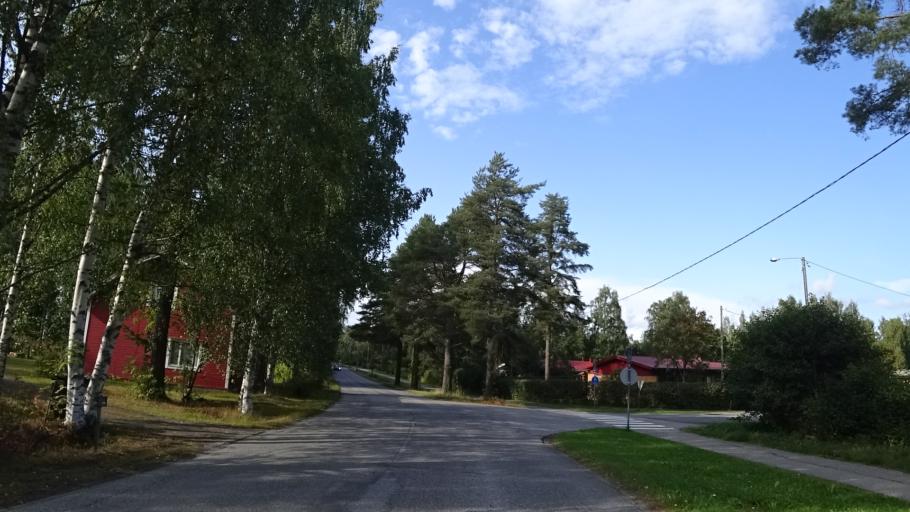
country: FI
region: North Karelia
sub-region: Pielisen Karjala
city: Lieksa
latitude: 63.3325
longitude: 30.0299
